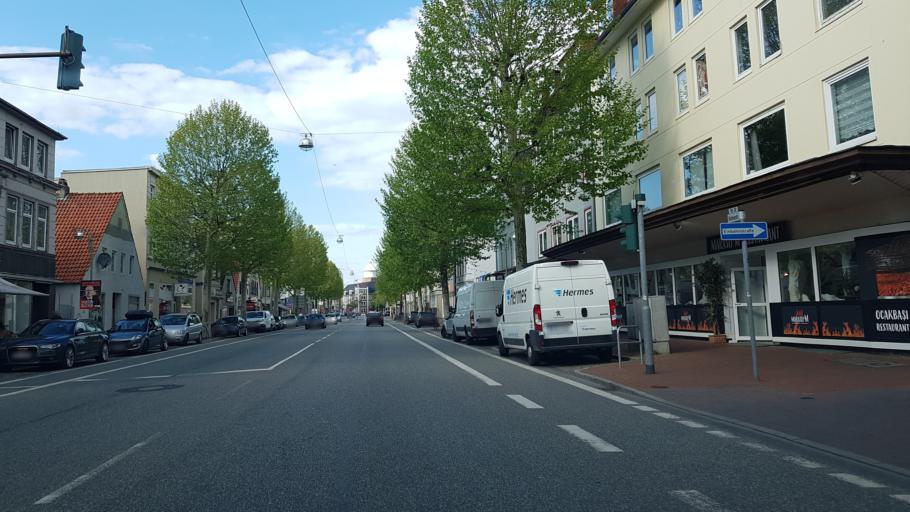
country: DE
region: Bremen
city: Bremerhaven
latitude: 53.5551
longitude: 8.5834
